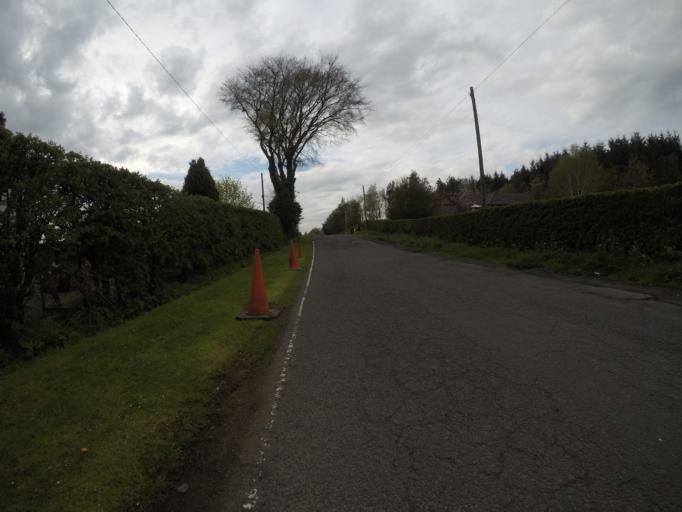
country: GB
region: Scotland
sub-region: East Ayrshire
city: Kilmarnock
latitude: 55.6408
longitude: -4.4762
